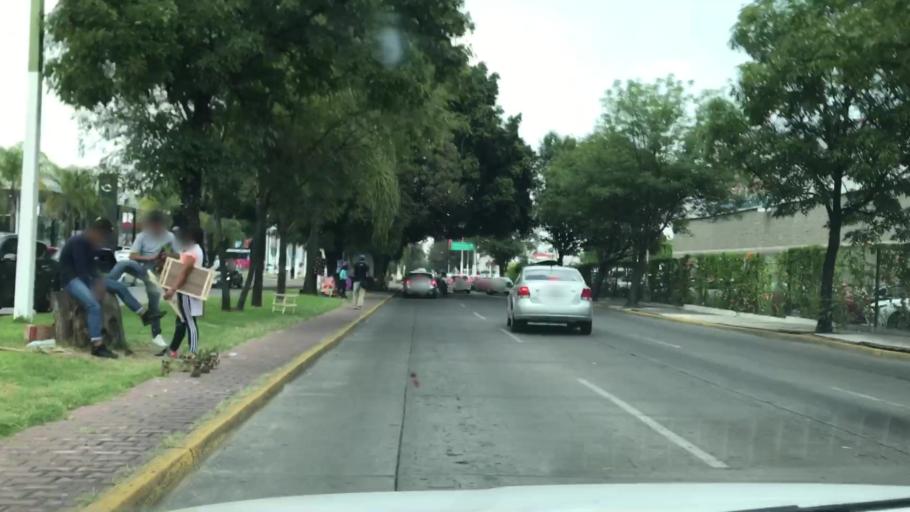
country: MX
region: Jalisco
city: Guadalajara
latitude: 20.6791
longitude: -103.4289
